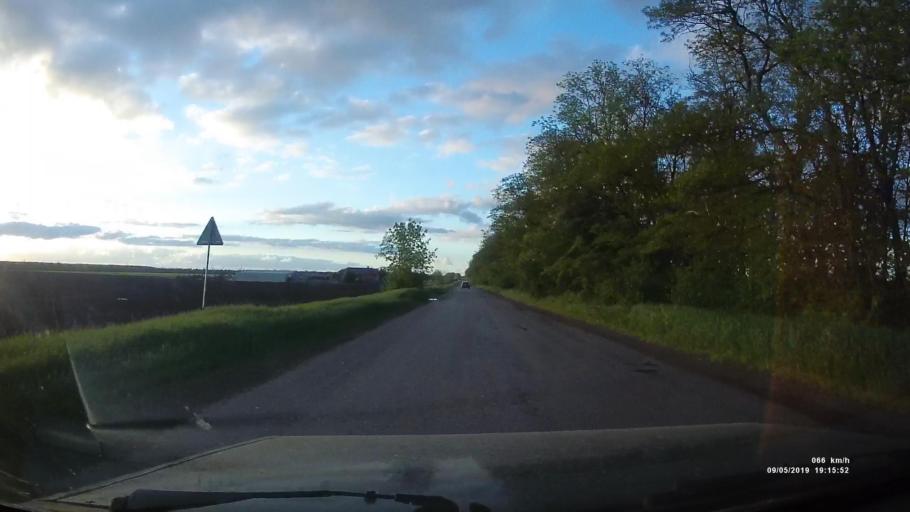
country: RU
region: Krasnodarskiy
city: Kanelovskaya
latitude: 46.7725
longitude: 39.2114
